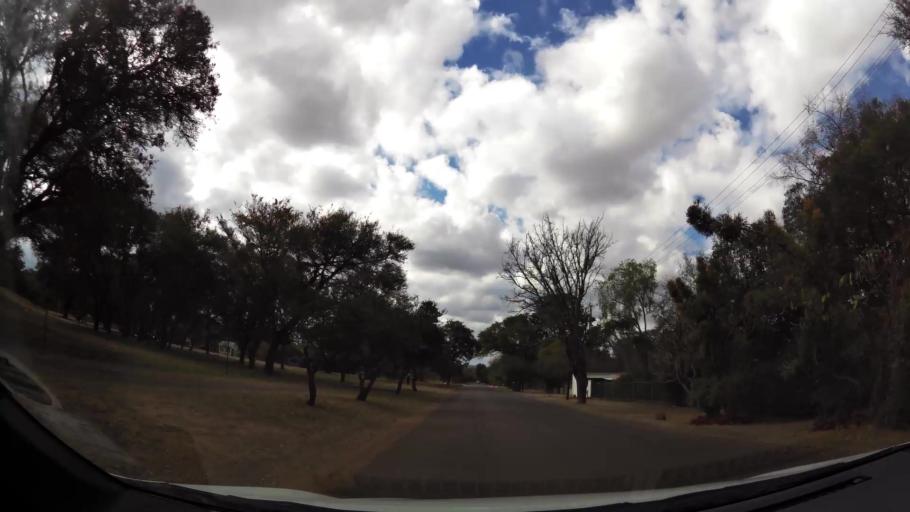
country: ZA
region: Limpopo
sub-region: Waterberg District Municipality
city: Modimolle
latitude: -24.7068
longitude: 28.4006
